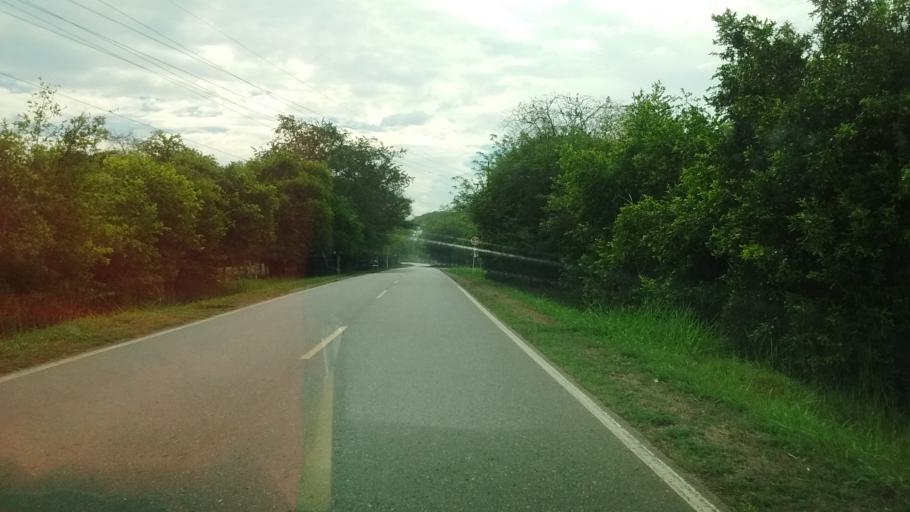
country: CO
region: Cauca
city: Caloto
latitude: 3.0473
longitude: -76.4408
